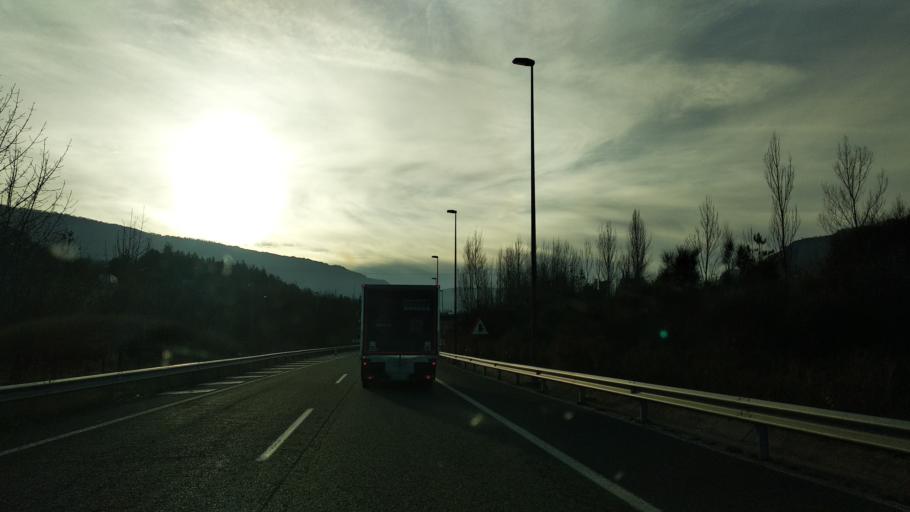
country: ES
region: Navarre
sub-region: Provincia de Navarra
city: Olazagutia
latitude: 42.8854
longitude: -2.1798
